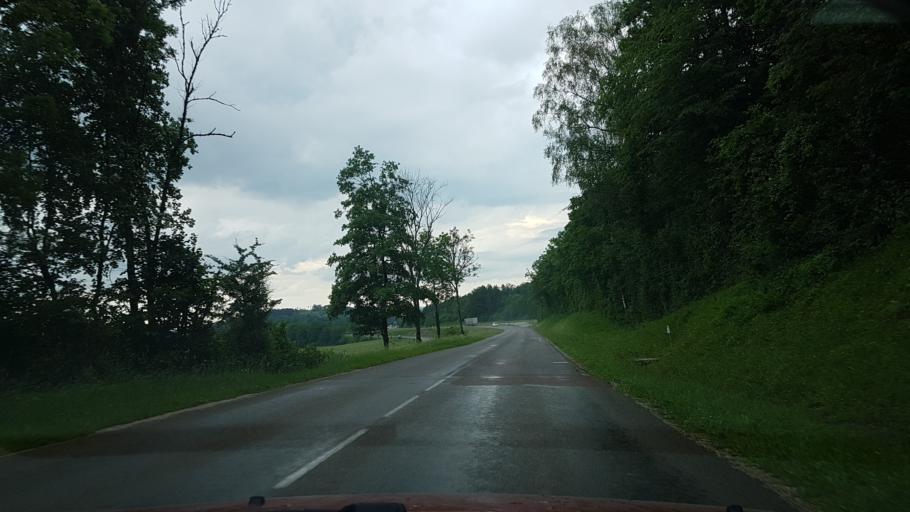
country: FR
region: Franche-Comte
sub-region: Departement du Jura
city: Clairvaux-les-Lacs
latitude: 46.5512
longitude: 5.7447
